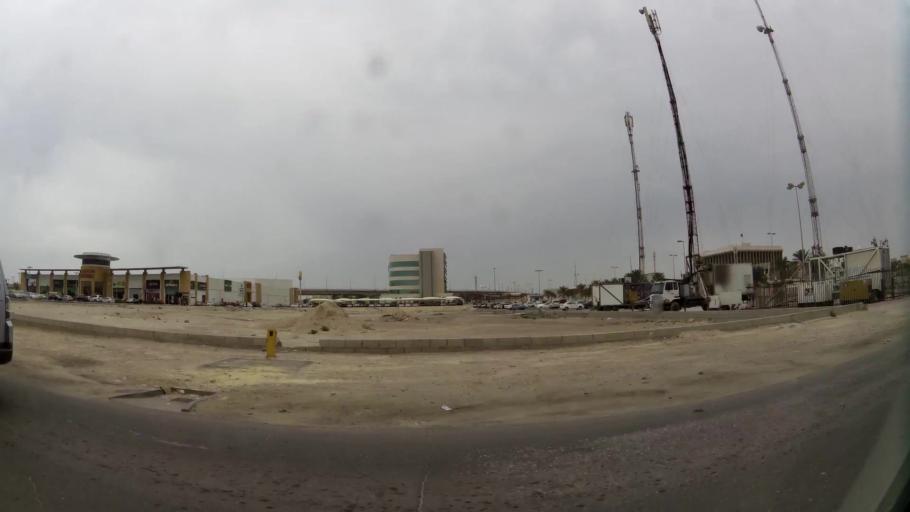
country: BH
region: Northern
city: Madinat `Isa
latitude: 26.1693
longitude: 50.5391
